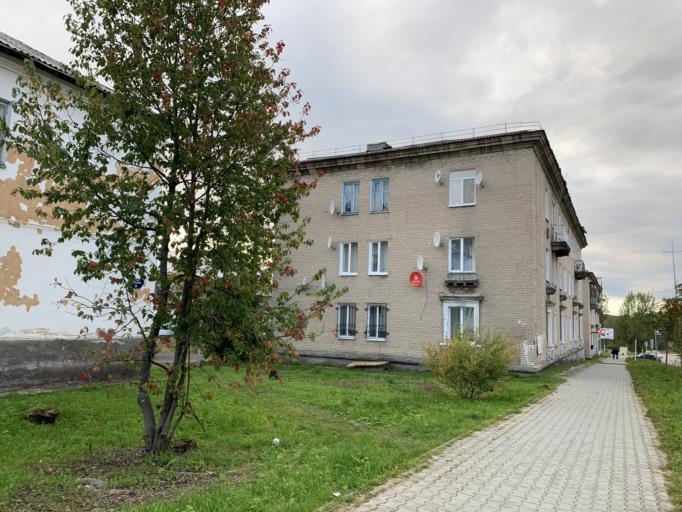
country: RU
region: Perm
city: Gubakha
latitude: 58.8447
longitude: 57.5488
